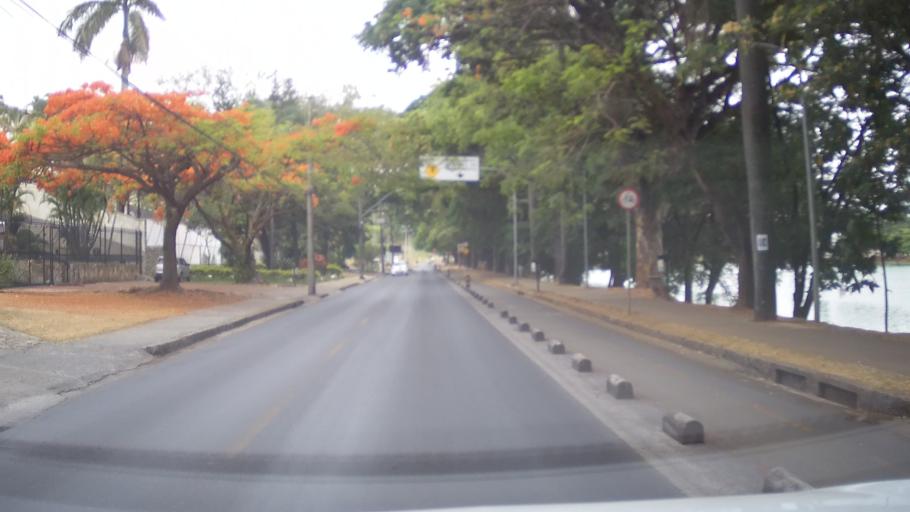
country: BR
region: Minas Gerais
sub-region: Belo Horizonte
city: Belo Horizonte
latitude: -19.8595
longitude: -43.9760
